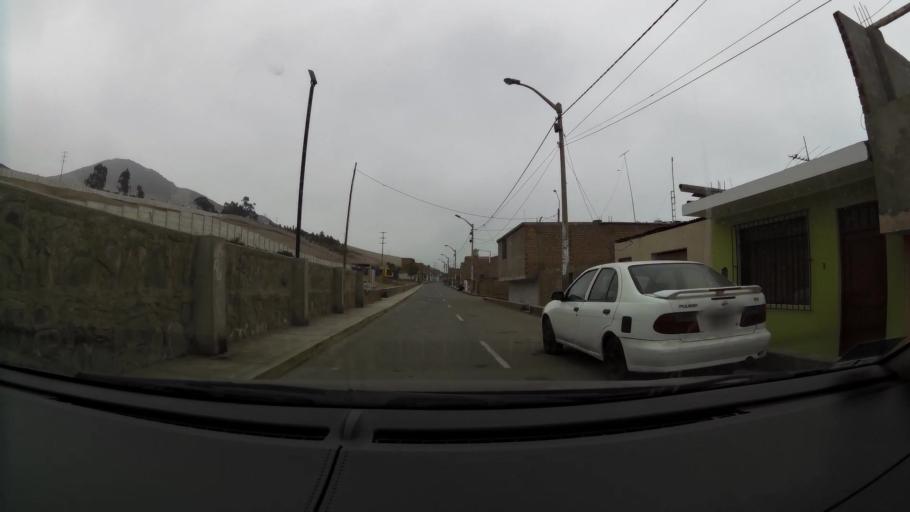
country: PE
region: Lima
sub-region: Provincia de Huaral
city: Chancay
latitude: -11.5981
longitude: -77.2504
